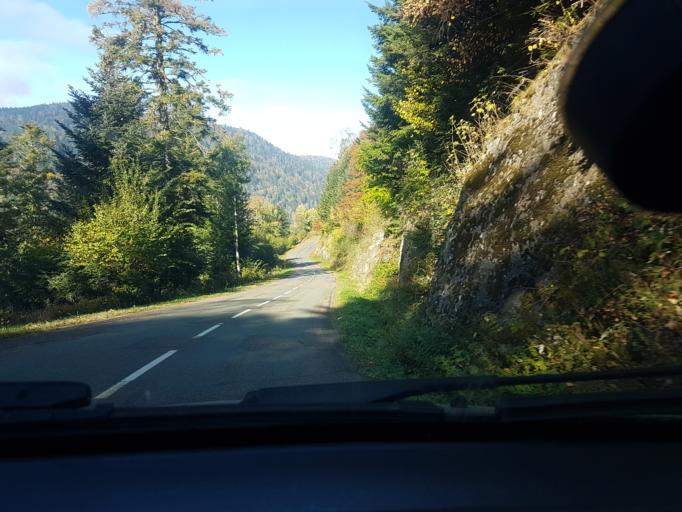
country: FR
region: Franche-Comte
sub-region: Departement de la Haute-Saone
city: Plancher-les-Mines
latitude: 47.7763
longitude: 6.7669
